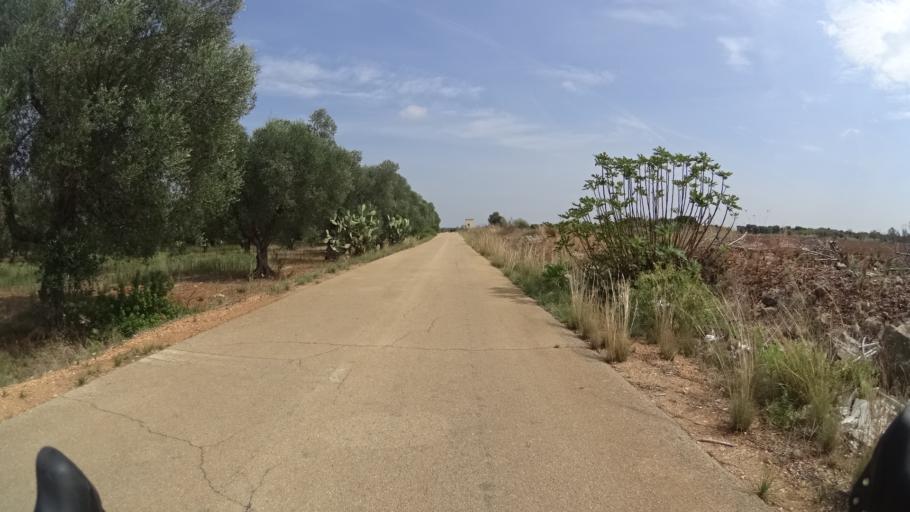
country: IT
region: Apulia
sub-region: Provincia di Brindisi
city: San Pancrazio Salentino
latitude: 40.3458
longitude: 17.8484
